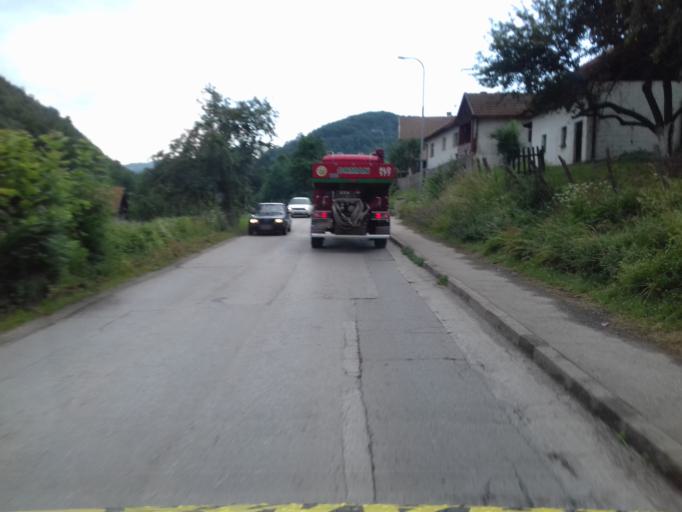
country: BA
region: Federation of Bosnia and Herzegovina
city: Visoko
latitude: 43.9678
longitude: 18.1838
